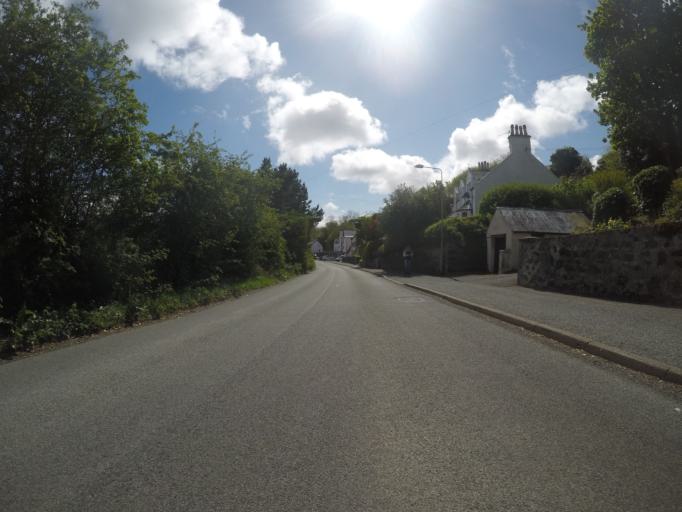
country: GB
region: Scotland
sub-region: Highland
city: Portree
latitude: 57.4166
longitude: -6.1912
